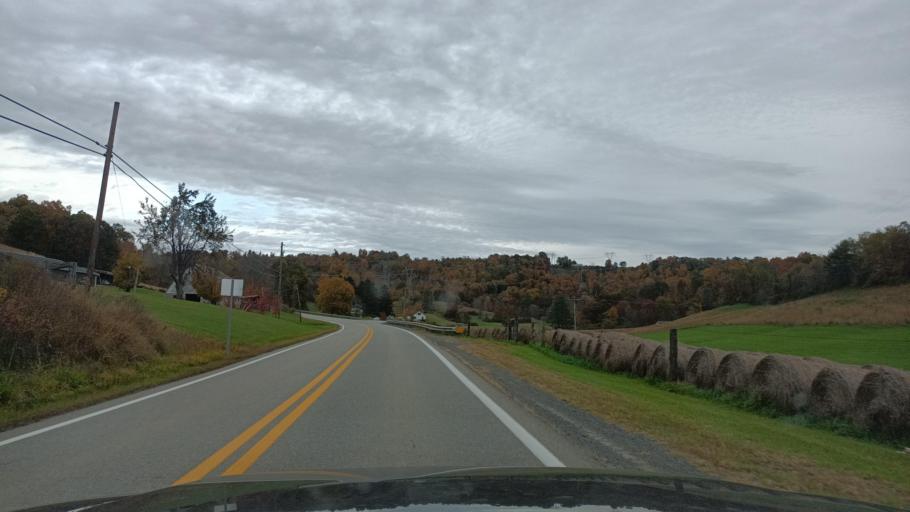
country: US
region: West Virginia
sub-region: Taylor County
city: Grafton
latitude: 39.3618
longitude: -79.9799
